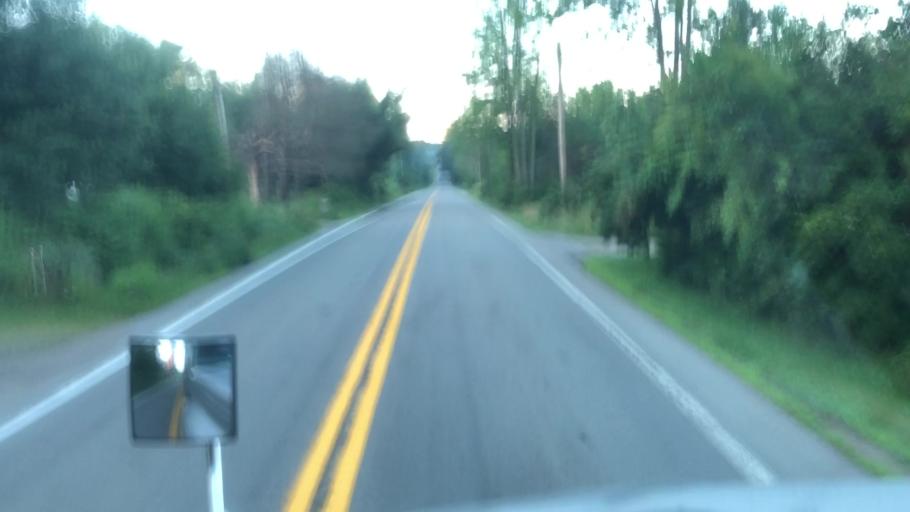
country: US
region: Pennsylvania
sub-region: Crawford County
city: Titusville
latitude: 41.5901
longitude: -79.6099
